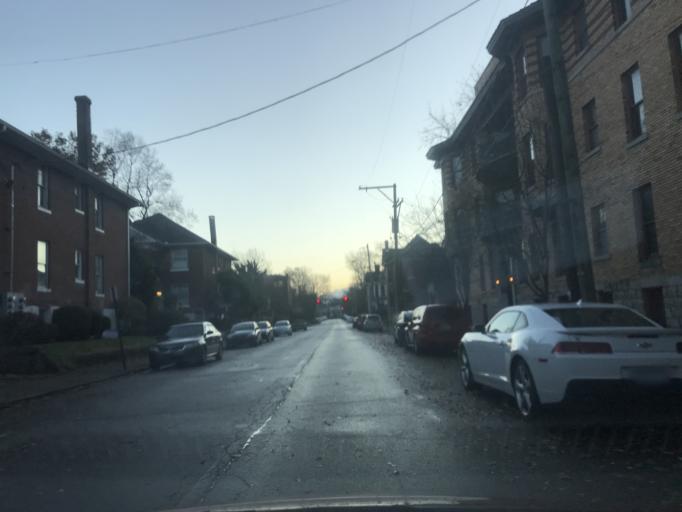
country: US
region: Kentucky
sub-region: Jefferson County
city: Louisville
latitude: 38.2286
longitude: -85.7560
